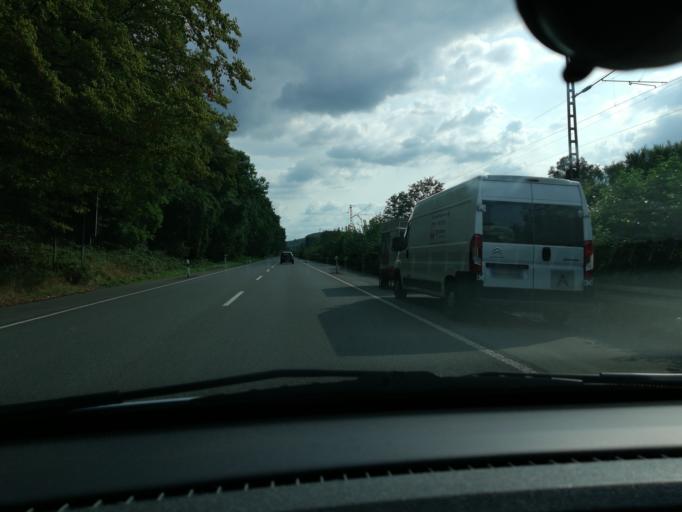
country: DE
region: North Rhine-Westphalia
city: Witten
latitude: 51.4199
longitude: 7.3538
